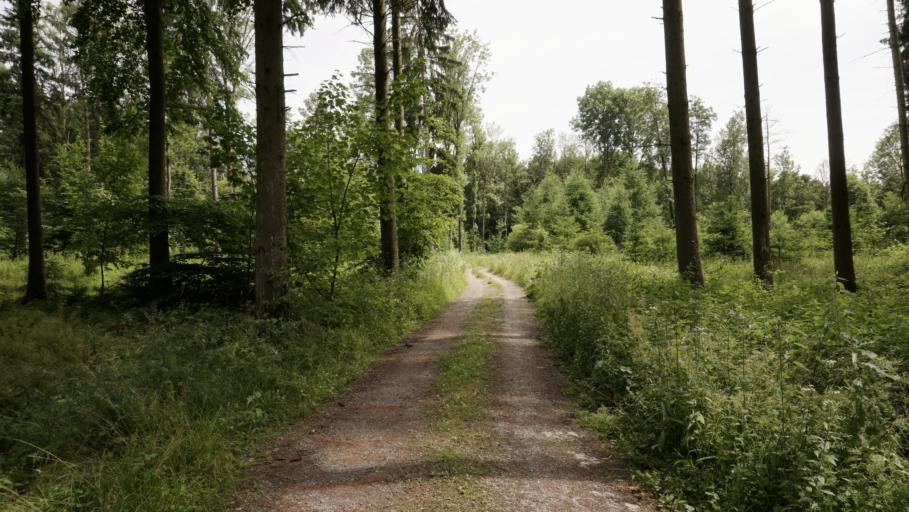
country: DE
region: Baden-Wuerttemberg
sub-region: Karlsruhe Region
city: Mosbach
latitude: 49.3350
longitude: 9.1898
